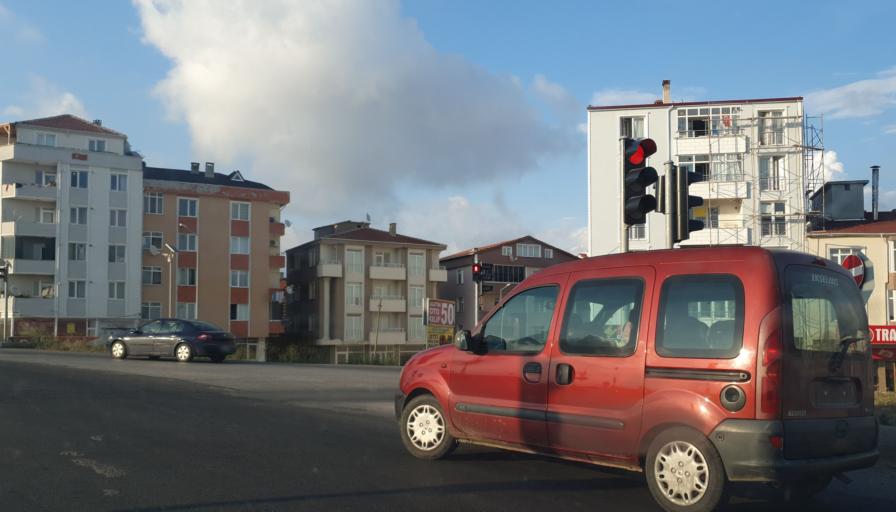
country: TR
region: Tekirdag
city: Cerkezkoey
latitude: 41.3317
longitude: 27.9699
